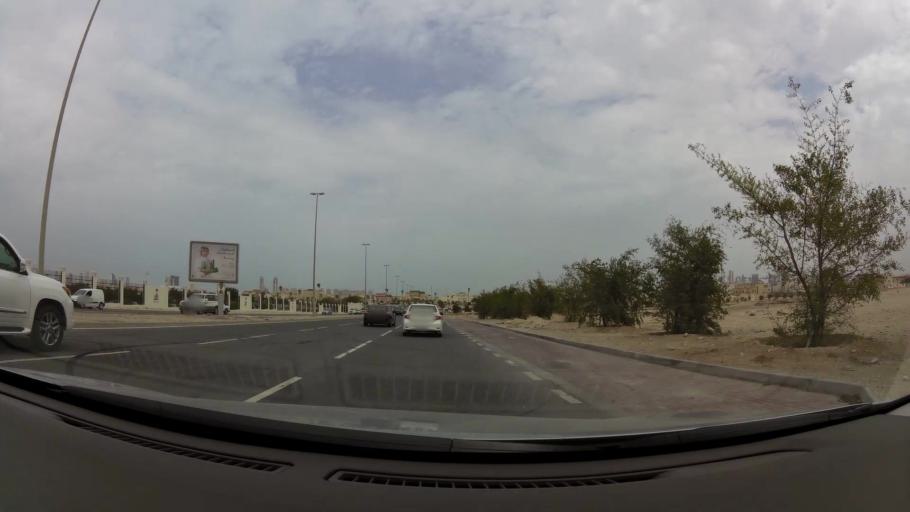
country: QA
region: Baladiyat ad Dawhah
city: Doha
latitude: 25.3578
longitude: 51.4915
